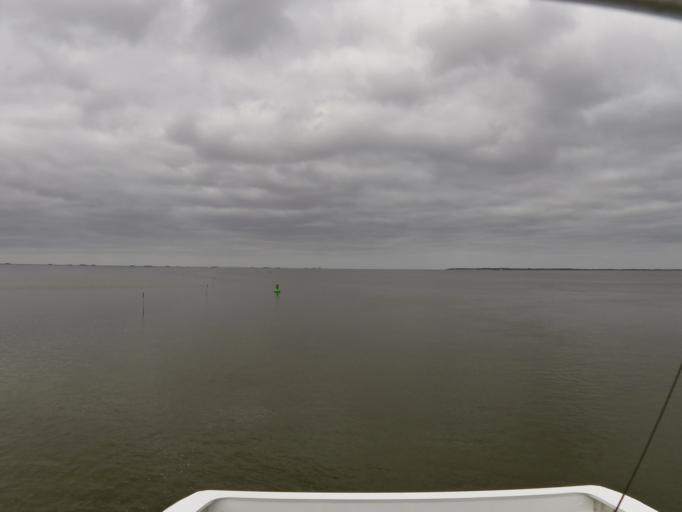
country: DE
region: Schleswig-Holstein
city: Dagebull
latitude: 54.7225
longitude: 8.6717
